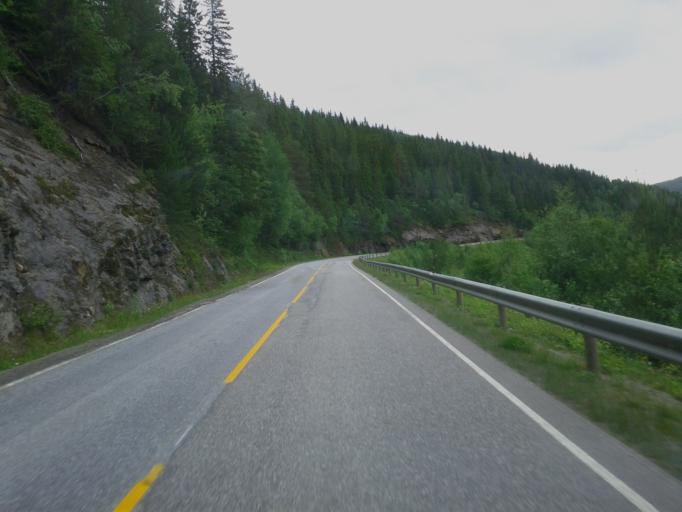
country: NO
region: Sor-Trondelag
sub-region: Holtalen
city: Alen
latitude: 62.8684
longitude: 11.2107
